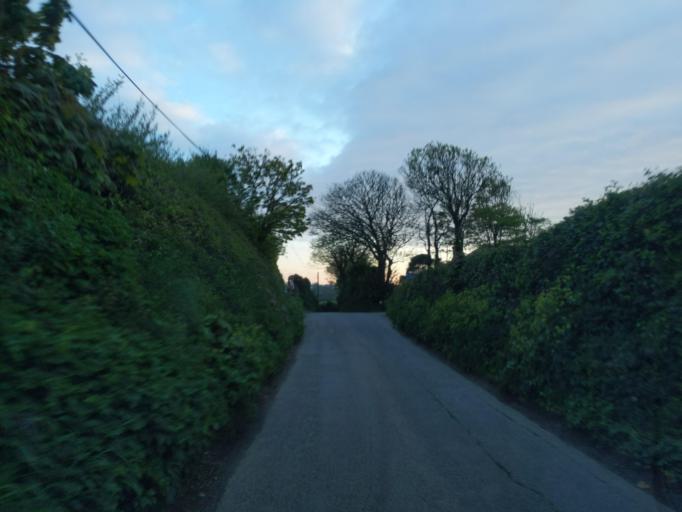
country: GB
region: England
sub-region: Cornwall
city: Polzeath
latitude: 50.5596
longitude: -4.8814
